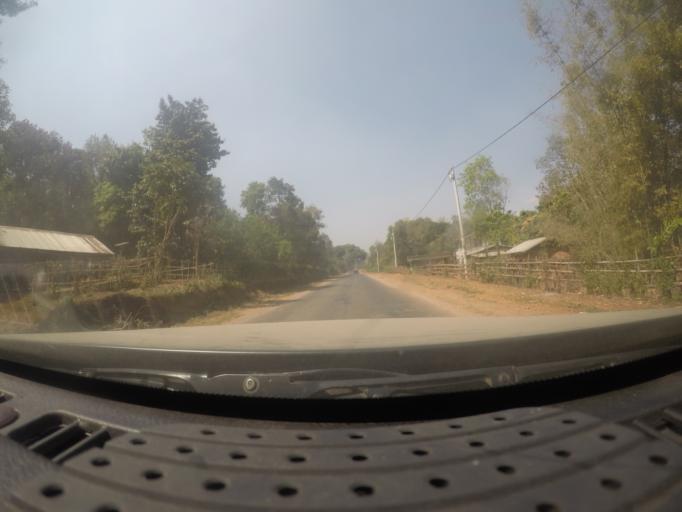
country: MM
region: Mandalay
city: Kyaukse
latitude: 21.1279
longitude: 96.4539
